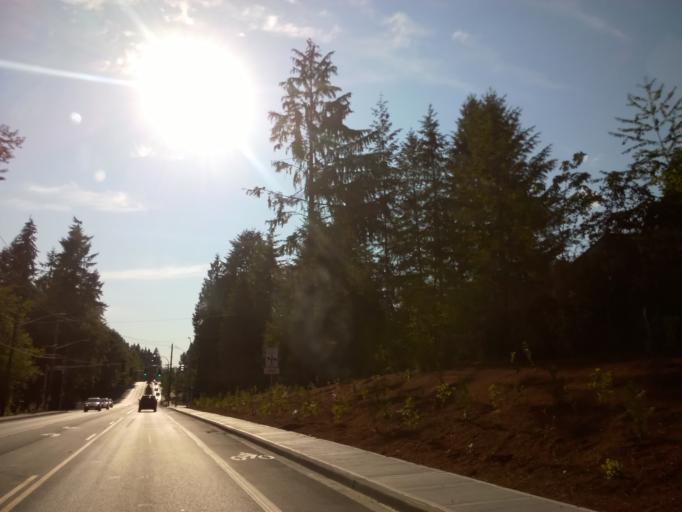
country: US
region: Washington
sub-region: King County
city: Woodinville
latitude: 47.7616
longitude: -122.1259
